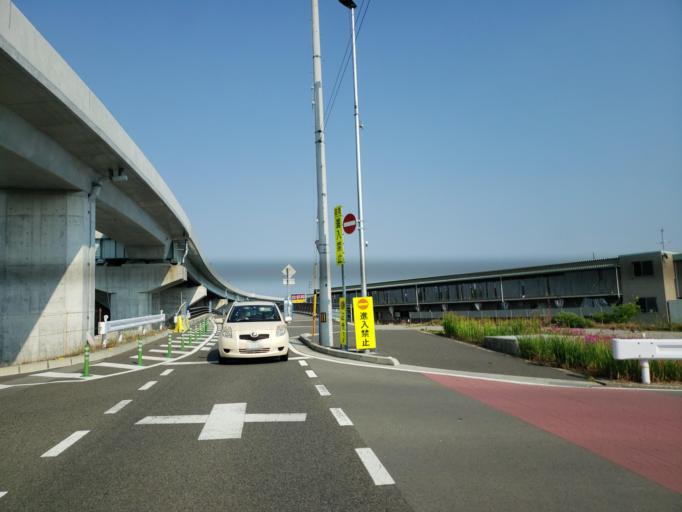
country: JP
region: Ehime
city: Masaki-cho
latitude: 33.8196
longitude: 132.7162
